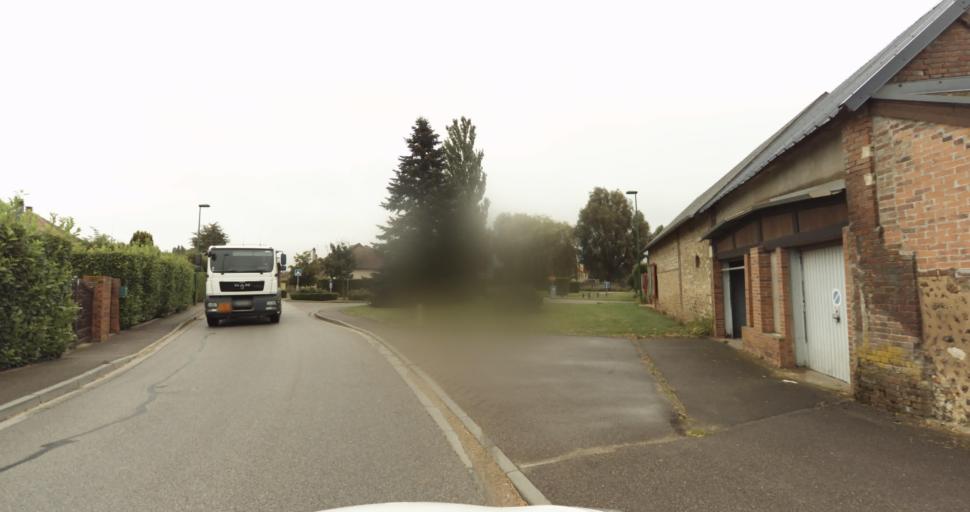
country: FR
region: Haute-Normandie
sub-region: Departement de l'Eure
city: Normanville
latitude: 49.0946
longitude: 1.1579
